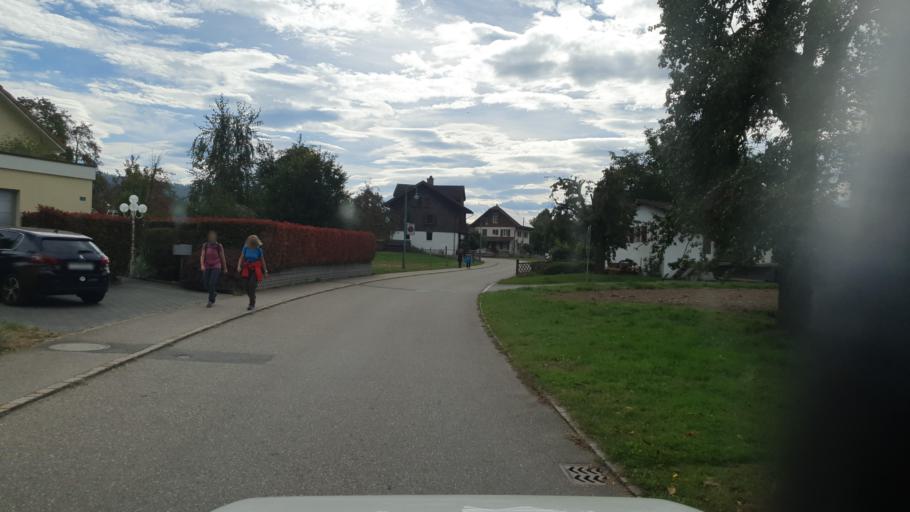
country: CH
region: Aargau
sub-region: Bezirk Lenzburg
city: Meisterschwanden
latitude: 47.2578
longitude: 8.2349
